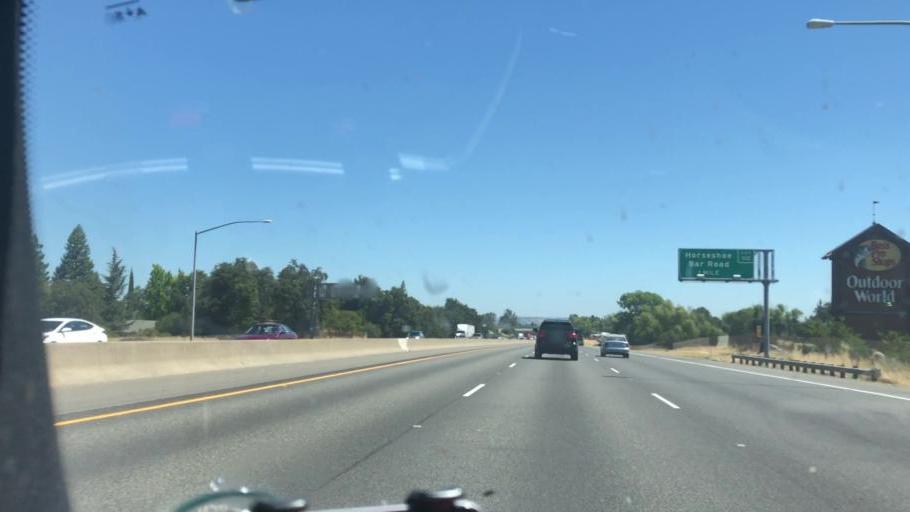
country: US
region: California
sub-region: Placer County
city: Loomis
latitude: 38.8061
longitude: -121.2016
